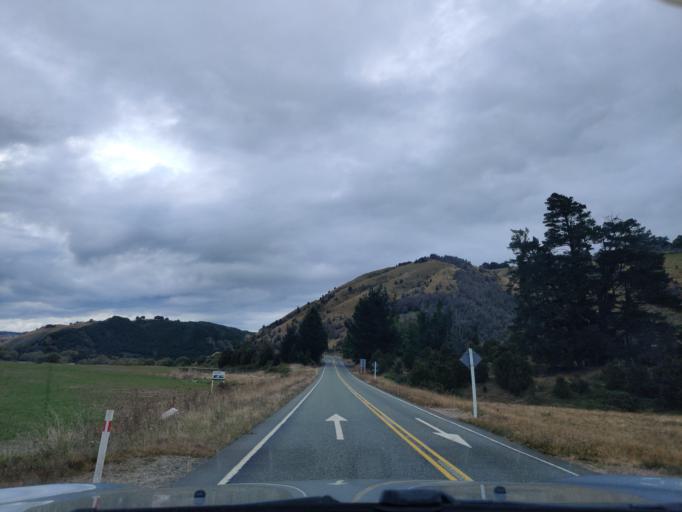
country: NZ
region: Tasman
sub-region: Tasman District
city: Wakefield
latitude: -41.7028
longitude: 172.6594
